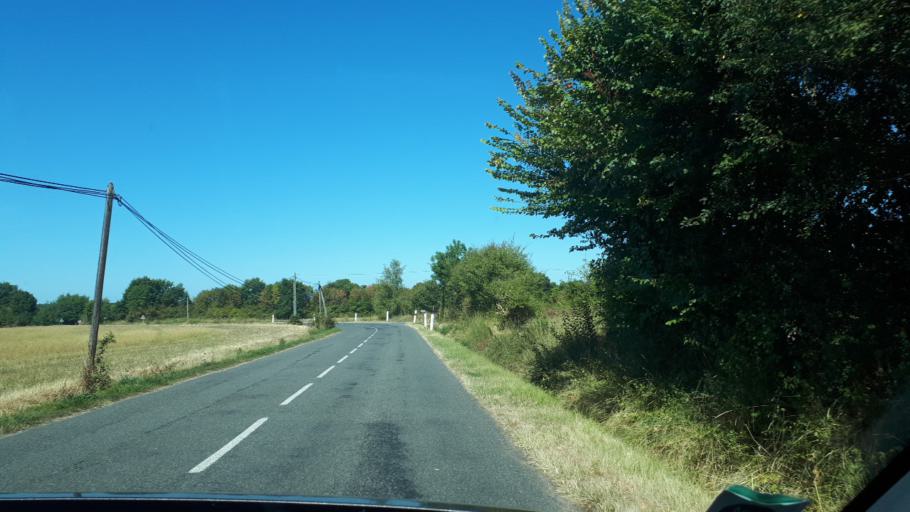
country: FR
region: Centre
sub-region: Departement du Loiret
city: Autry-le-Chatel
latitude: 47.6027
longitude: 2.5961
